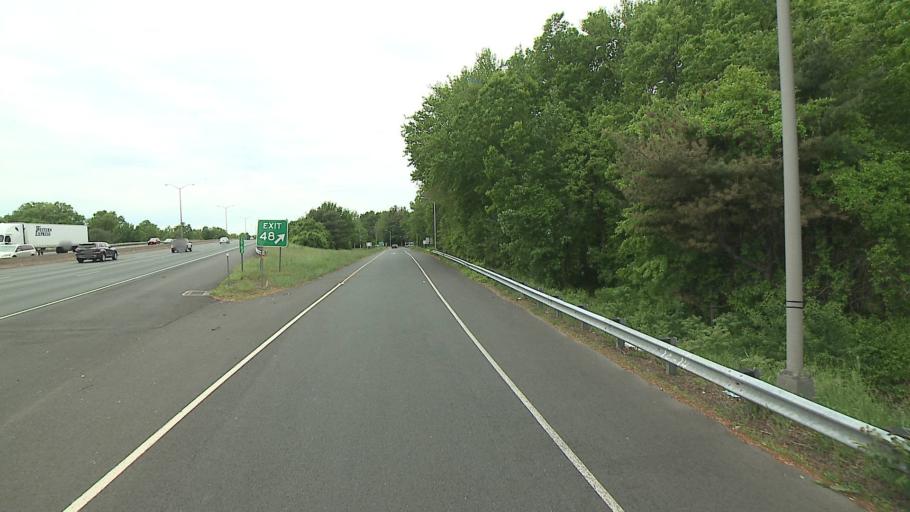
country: US
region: Connecticut
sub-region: Hartford County
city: Thompsonville
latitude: 41.9996
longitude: -72.5856
